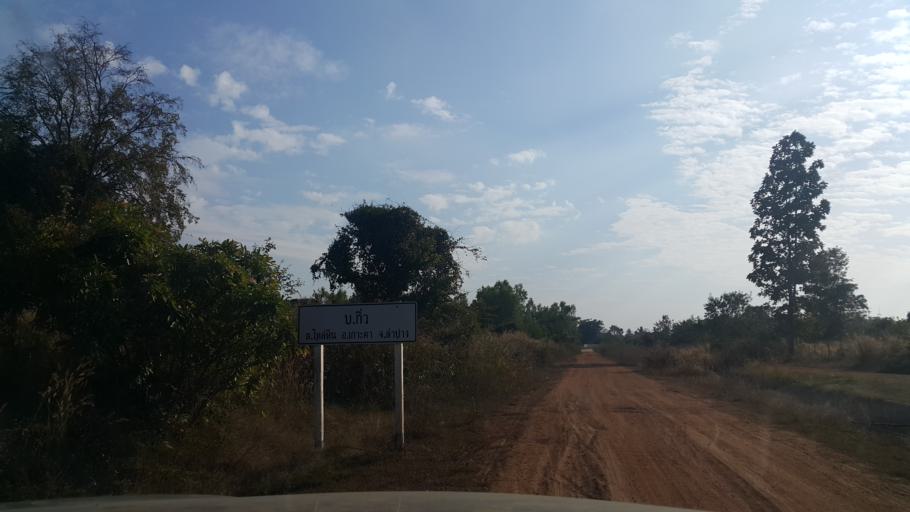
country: TH
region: Lampang
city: Ko Kha
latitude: 18.2349
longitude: 99.3573
